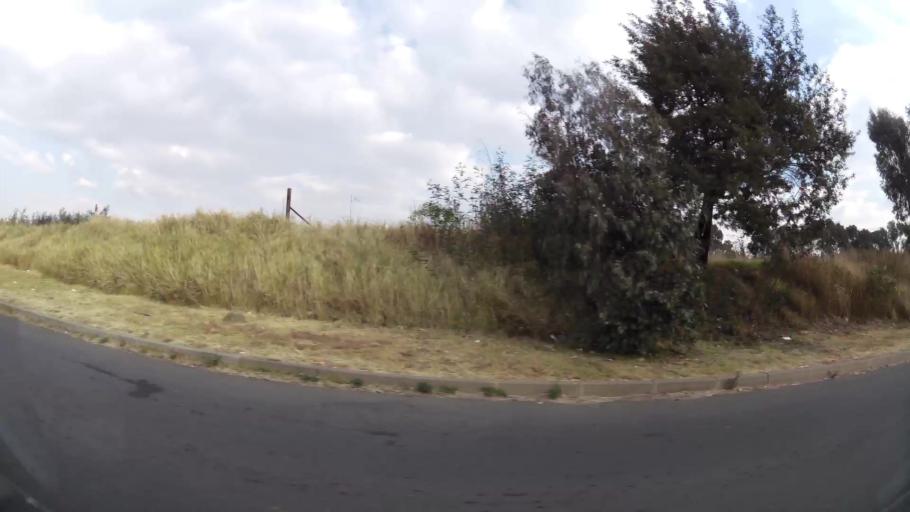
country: ZA
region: Gauteng
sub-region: City of Johannesburg Metropolitan Municipality
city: Modderfontein
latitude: -26.1535
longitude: 28.1864
